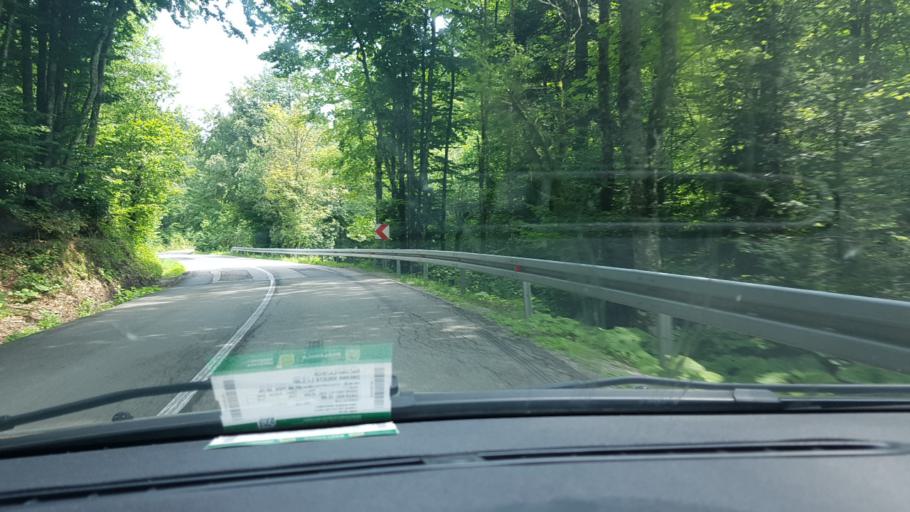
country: HR
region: Primorsko-Goranska
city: Hreljin
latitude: 45.3332
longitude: 14.6786
